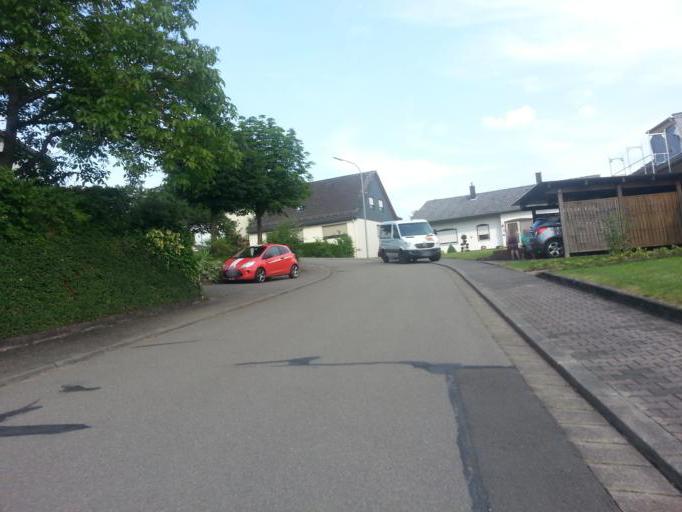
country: DE
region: Saarland
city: Oberthal
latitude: 49.5165
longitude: 7.1102
